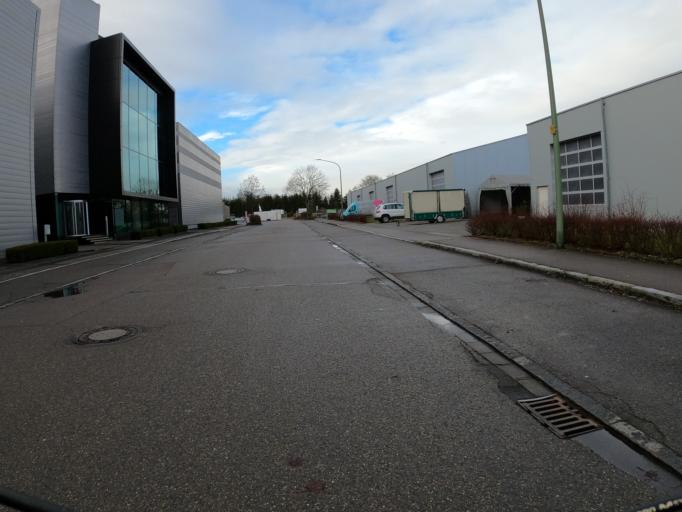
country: DE
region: Bavaria
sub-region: Swabia
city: Holzheim
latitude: 48.4243
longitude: 10.0664
